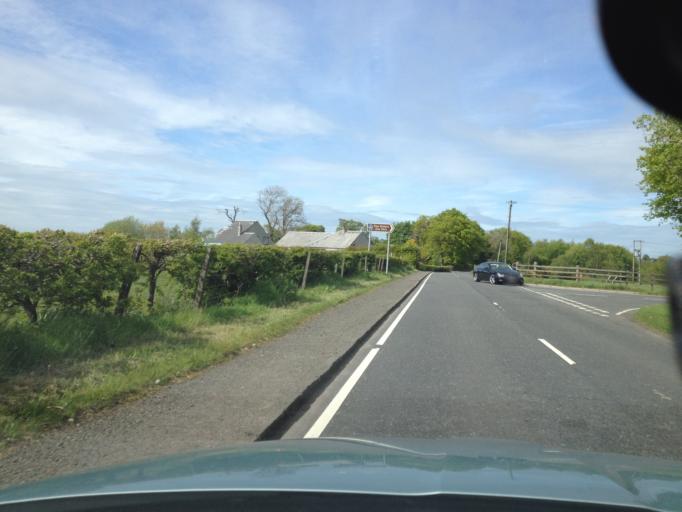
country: GB
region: Scotland
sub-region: West Lothian
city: West Calder
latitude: 55.8600
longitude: -3.5706
